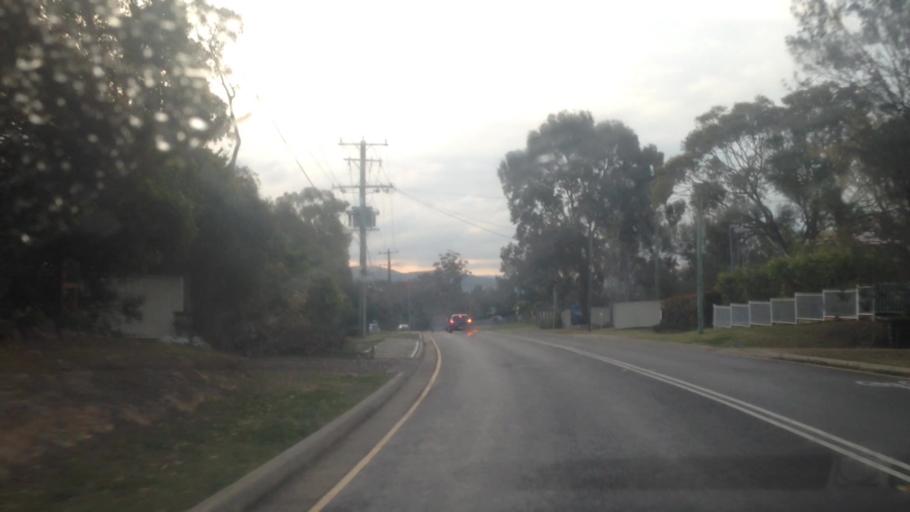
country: AU
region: New South Wales
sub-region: Wyong Shire
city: Charmhaven
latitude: -33.1857
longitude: 151.4915
